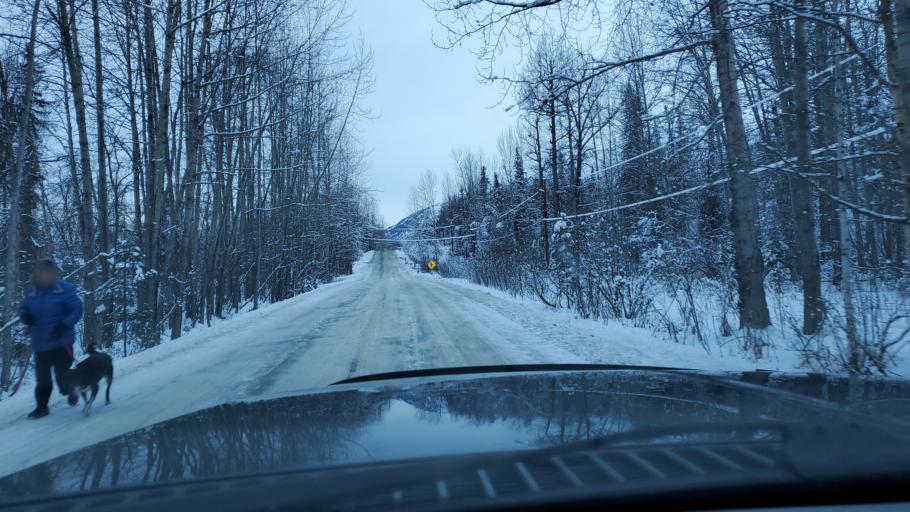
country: US
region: Alaska
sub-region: Matanuska-Susitna Borough
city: Lakes
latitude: 61.6933
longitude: -149.3082
